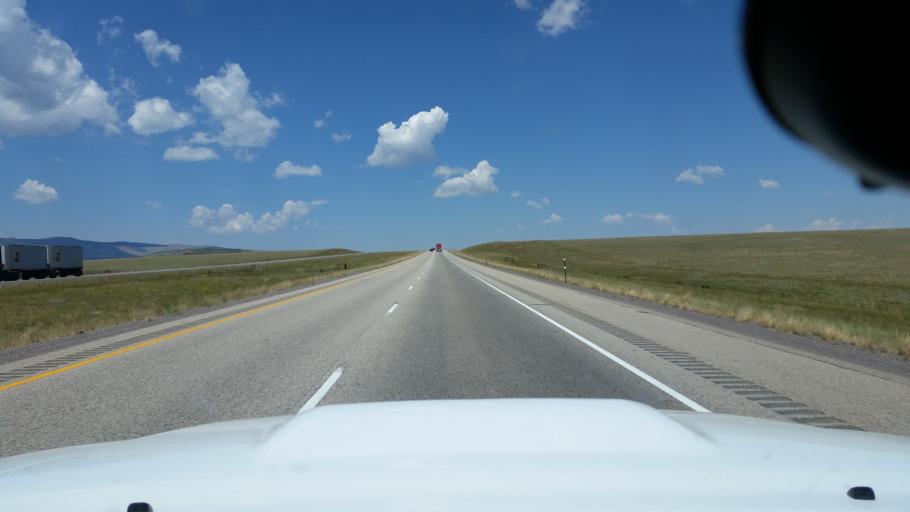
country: US
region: Wyoming
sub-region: Albany County
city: Laramie
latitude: 41.4669
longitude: -105.9913
